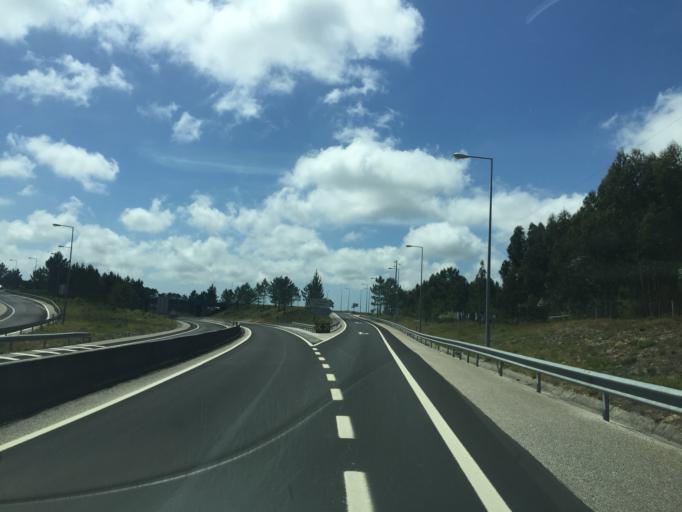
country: PT
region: Leiria
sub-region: Marinha Grande
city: Marinha Grande
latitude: 39.7152
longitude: -8.9214
